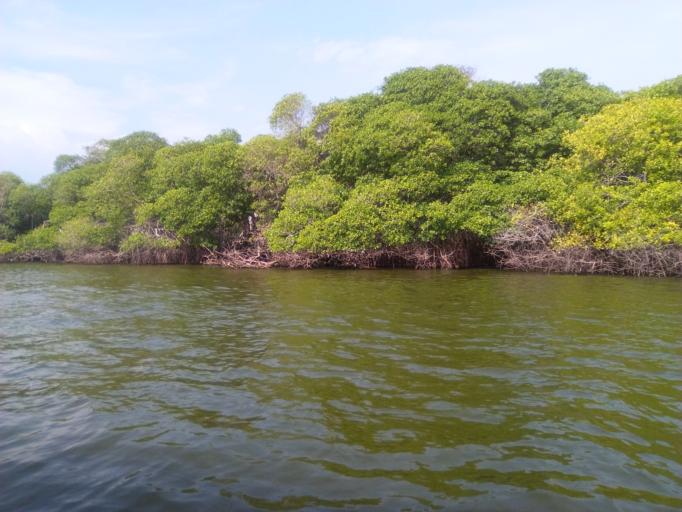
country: MX
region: Guerrero
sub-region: Coyuca de Benitez
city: Colonia Luces en el Mar
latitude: 16.9054
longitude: -99.9708
